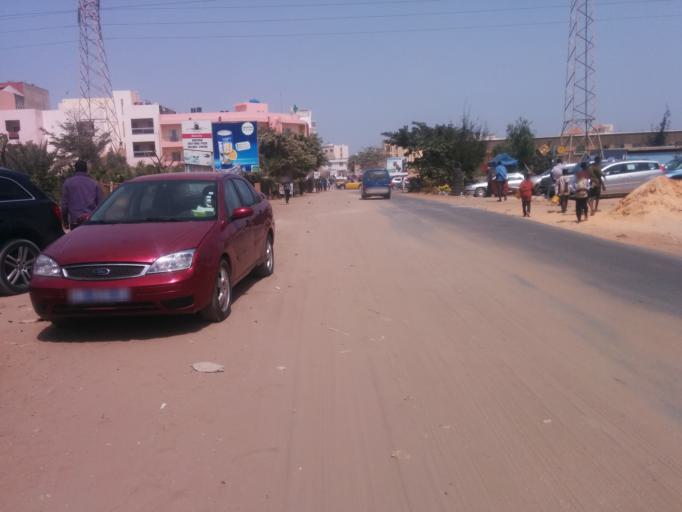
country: SN
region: Dakar
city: Grand Dakar
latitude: 14.7362
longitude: -17.4337
